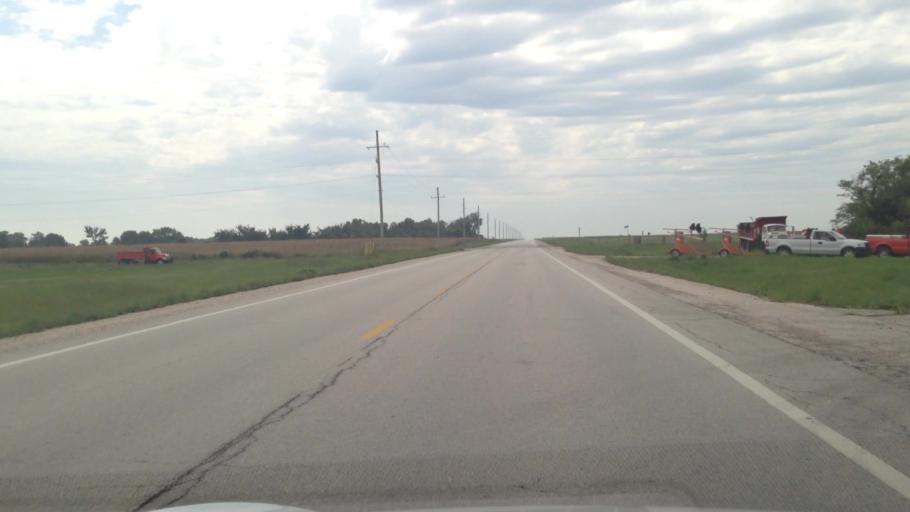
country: US
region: Kansas
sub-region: Anderson County
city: Garnett
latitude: 38.0681
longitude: -95.1694
